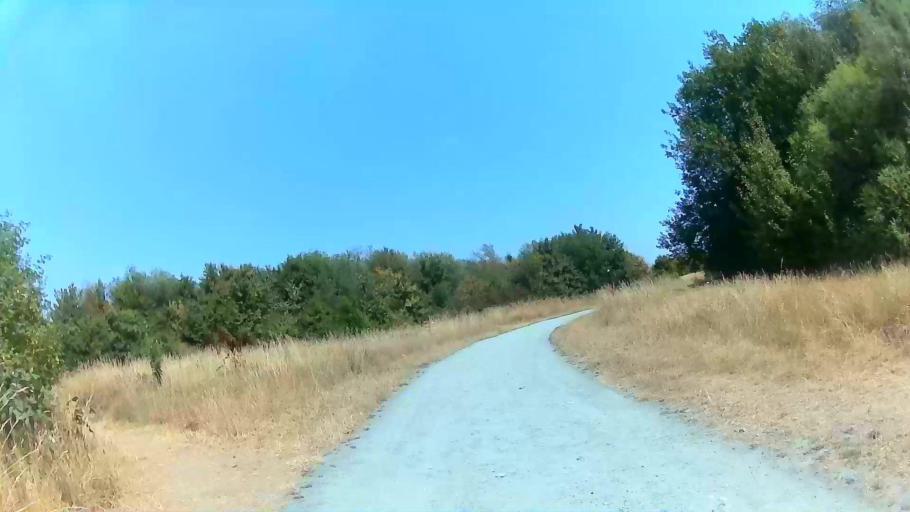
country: GB
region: England
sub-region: Greater London
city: Elm Park
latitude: 51.5304
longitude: 0.1923
